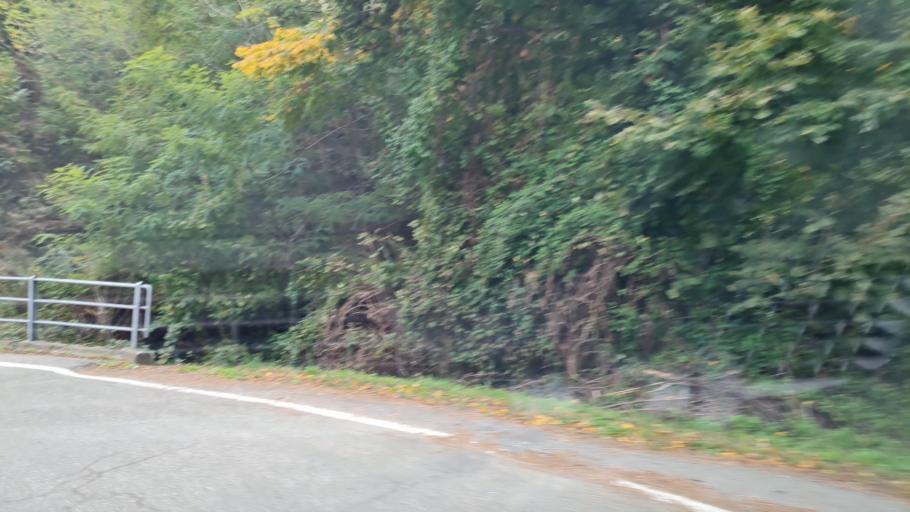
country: IT
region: Piedmont
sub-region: Provincia di Biella
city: Mezzana Mortigliengo
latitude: 45.6275
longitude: 8.1831
